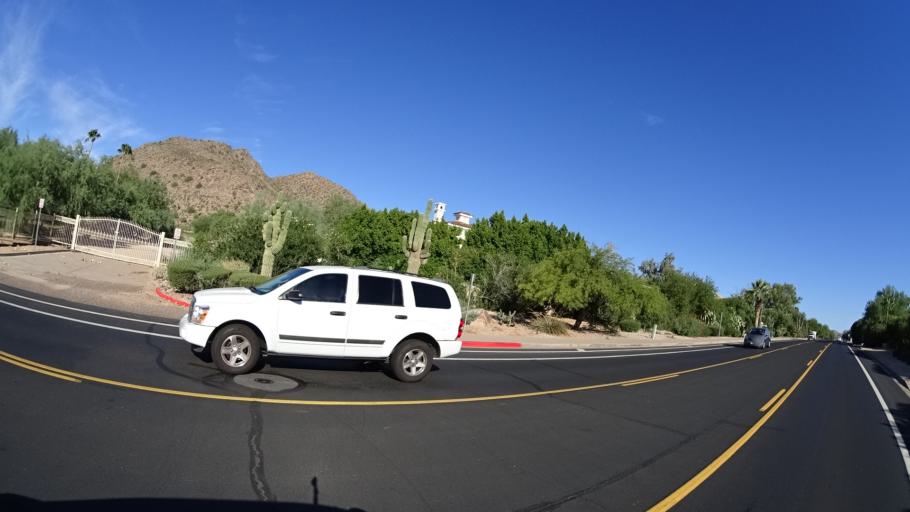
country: US
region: Arizona
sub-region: Maricopa County
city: Paradise Valley
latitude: 33.5113
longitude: -111.9432
